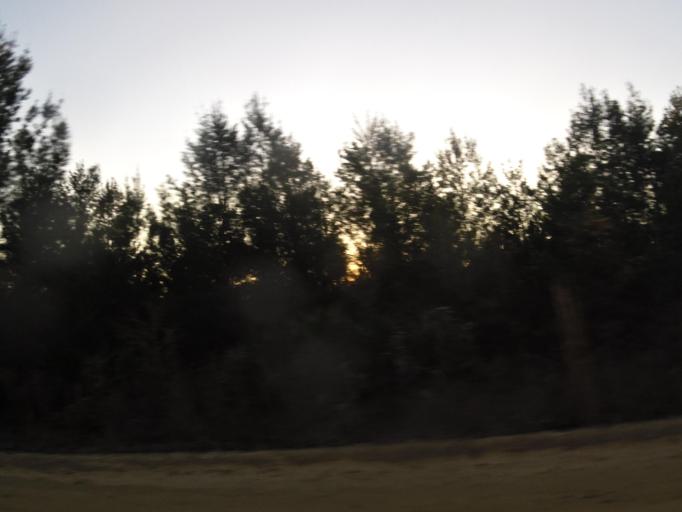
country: US
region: Florida
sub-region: Clay County
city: Green Cove Springs
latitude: 29.9260
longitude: -81.7810
